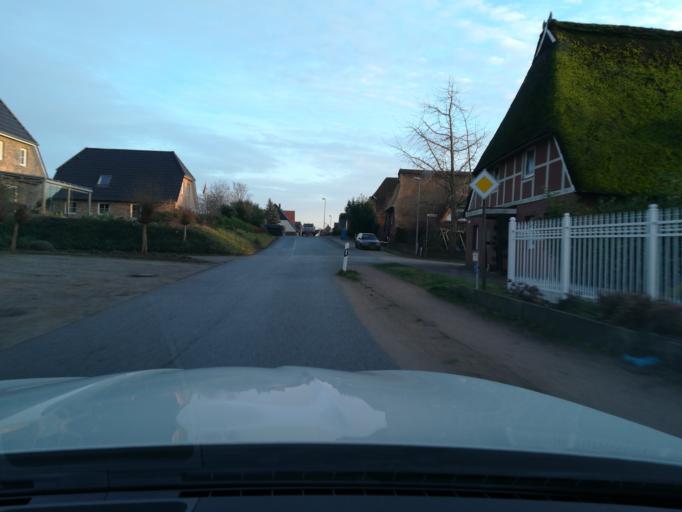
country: DE
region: Lower Saxony
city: Stelle
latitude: 53.4191
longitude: 10.1271
